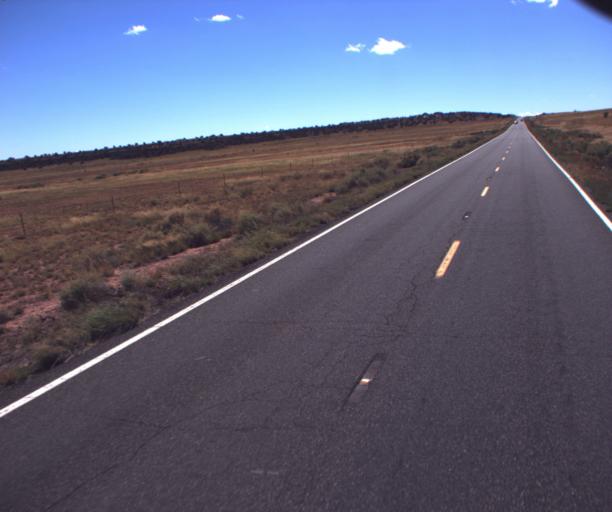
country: US
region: Arizona
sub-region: Apache County
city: Saint Johns
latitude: 34.7654
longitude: -109.2416
